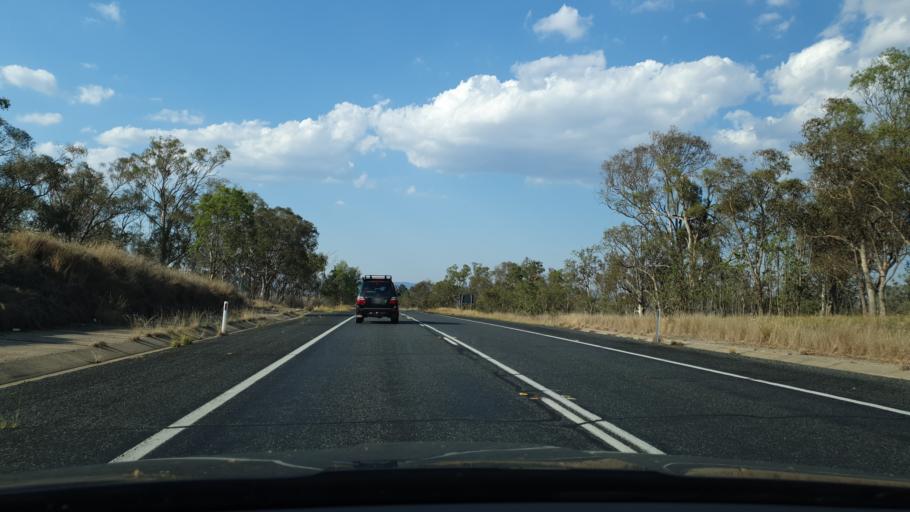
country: AU
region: New South Wales
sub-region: Tenterfield Municipality
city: Carrolls Creek
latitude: -29.1033
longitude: 152.0007
